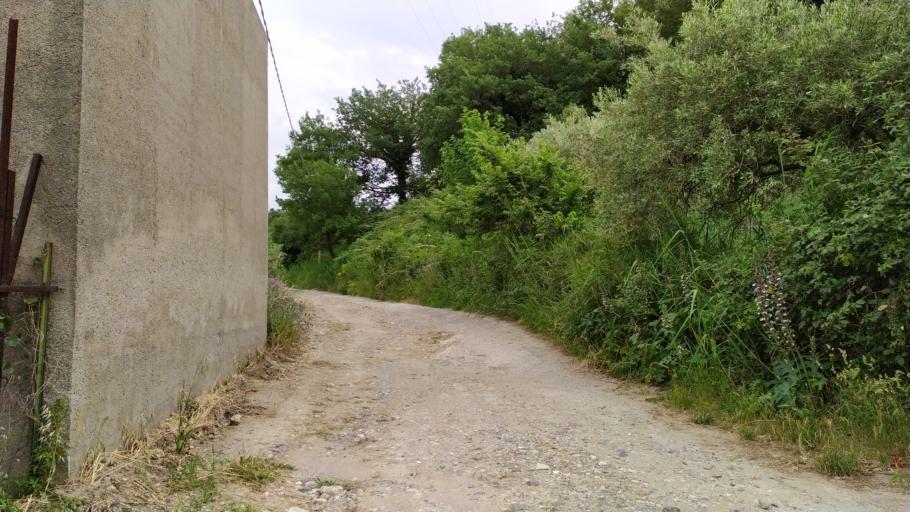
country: IT
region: Sicily
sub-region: Messina
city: Gualtieri Sicamino
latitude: 38.1568
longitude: 15.2984
